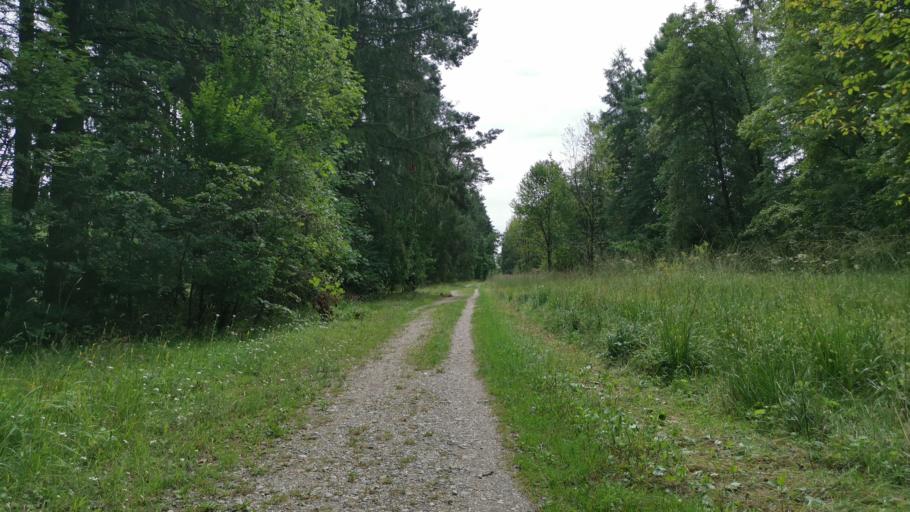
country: DE
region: Bavaria
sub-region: Upper Bavaria
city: Unterhaching
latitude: 48.0748
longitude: 11.5739
